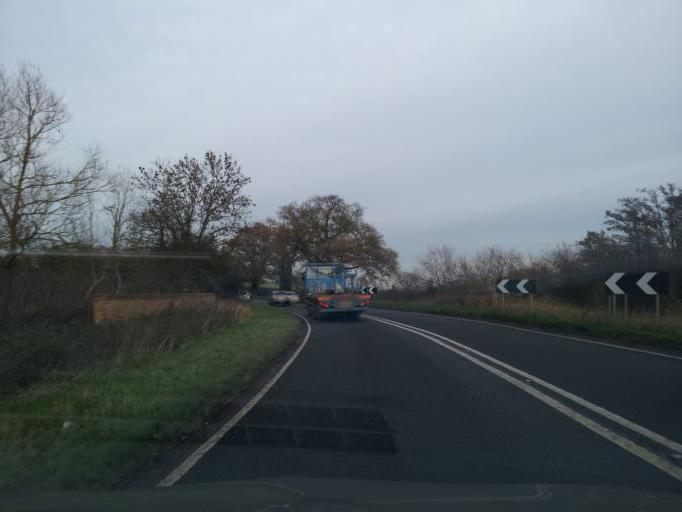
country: GB
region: England
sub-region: Buckinghamshire
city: Stewkley
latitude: 51.8812
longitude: -0.7332
